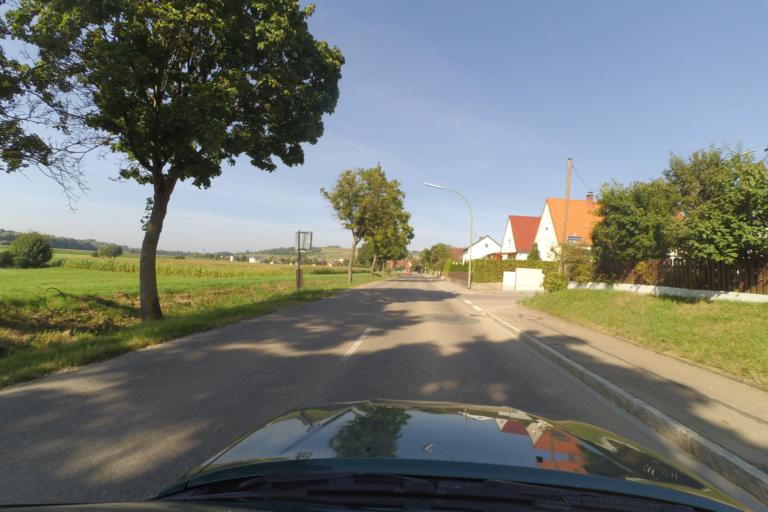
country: DE
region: Bavaria
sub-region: Swabia
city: Asbach-Baumenheim
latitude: 48.7203
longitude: 10.8175
